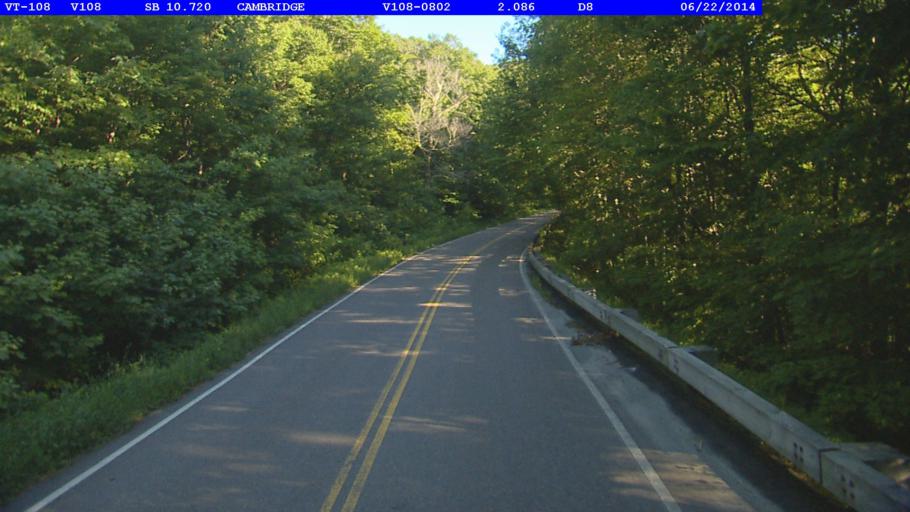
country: US
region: Vermont
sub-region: Lamoille County
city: Johnson
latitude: 44.5667
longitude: -72.7840
